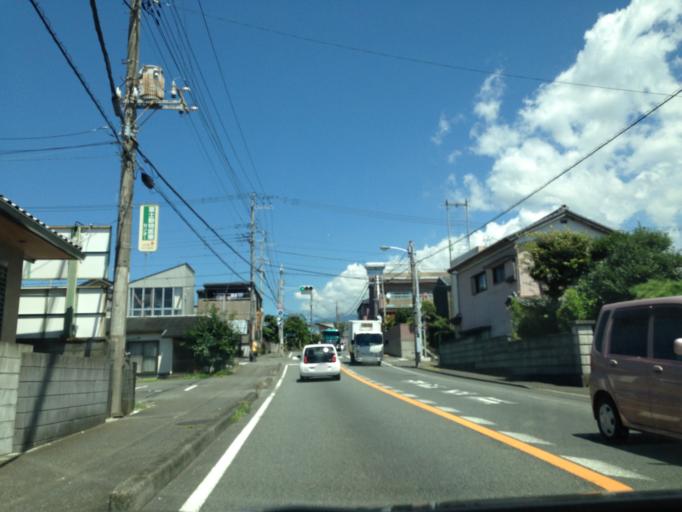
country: JP
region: Shizuoka
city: Fuji
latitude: 35.1653
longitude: 138.6889
